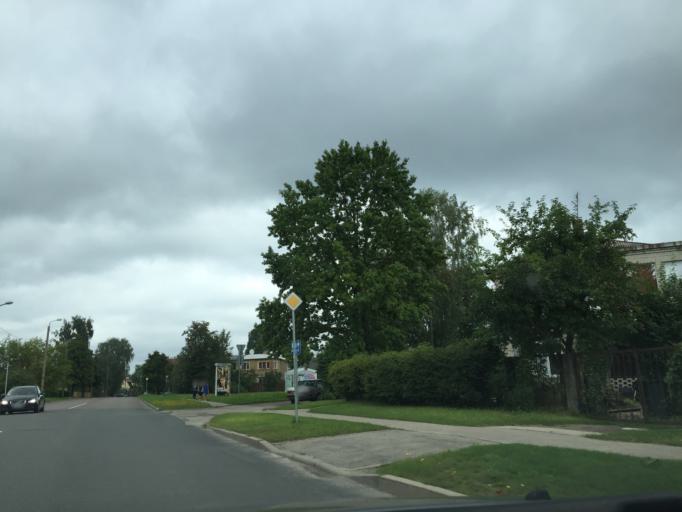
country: LV
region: Riga
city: Bergi
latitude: 56.9824
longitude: 24.2410
